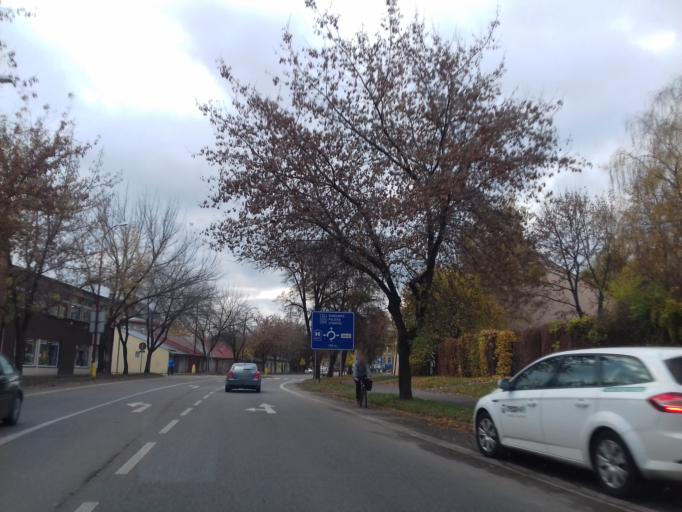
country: CZ
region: Pardubicky
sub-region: Okres Svitavy
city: Svitavy
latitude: 49.7544
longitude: 16.4721
